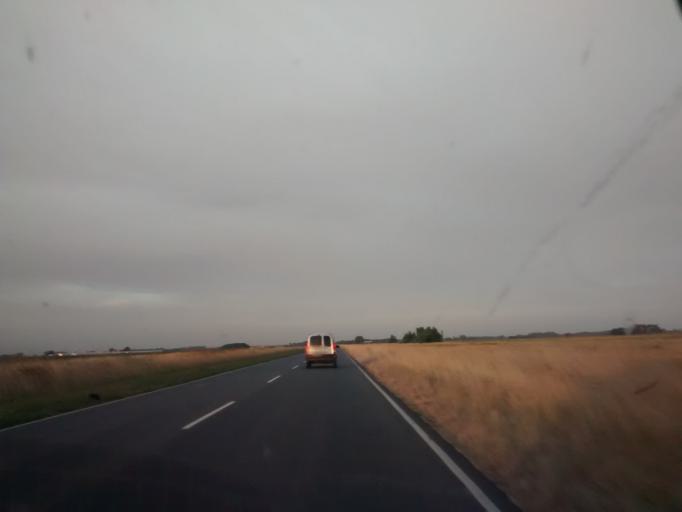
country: AR
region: Buenos Aires
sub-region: Partido de General Belgrano
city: General Belgrano
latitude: -35.8250
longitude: -58.5768
